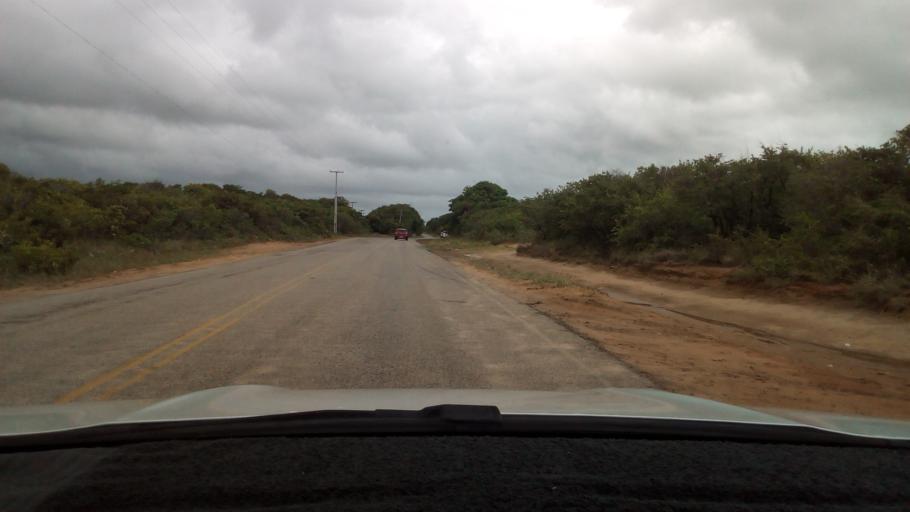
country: BR
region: Paraiba
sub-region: Pitimbu
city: Pitimbu
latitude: -7.3636
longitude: -34.8007
